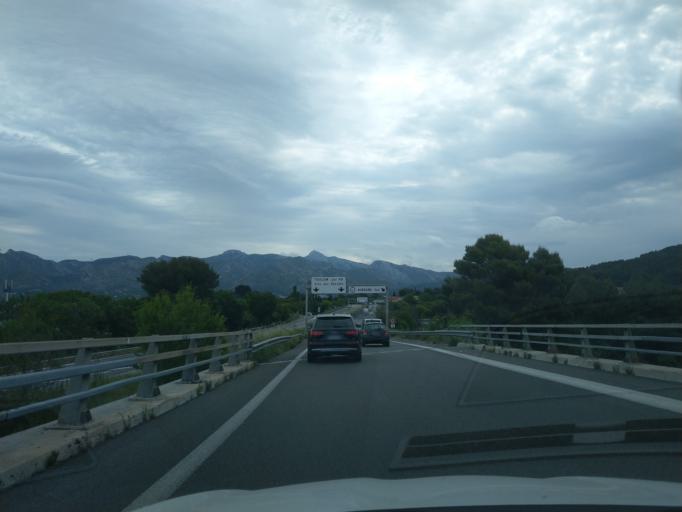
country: FR
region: Provence-Alpes-Cote d'Azur
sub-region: Departement des Bouches-du-Rhone
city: Aubagne
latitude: 43.2828
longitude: 5.5787
